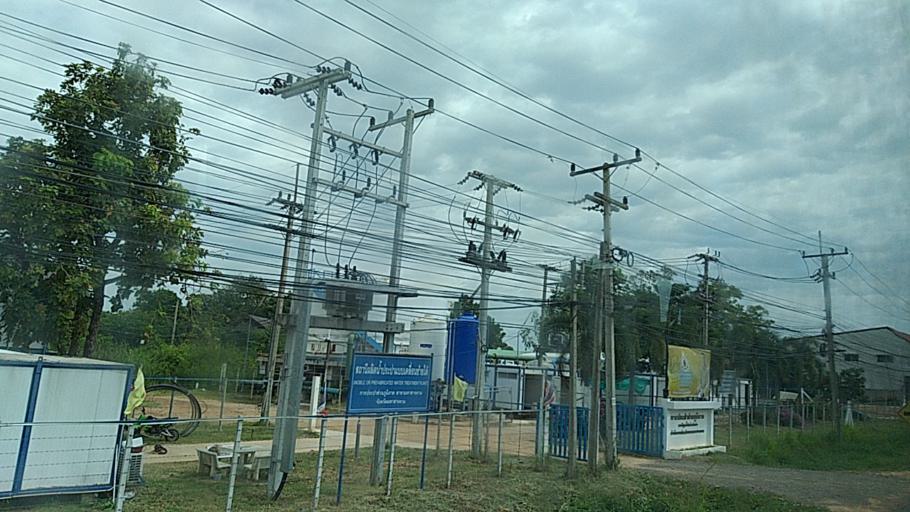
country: TH
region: Maha Sarakham
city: Maha Sarakham
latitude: 16.2166
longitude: 103.2774
